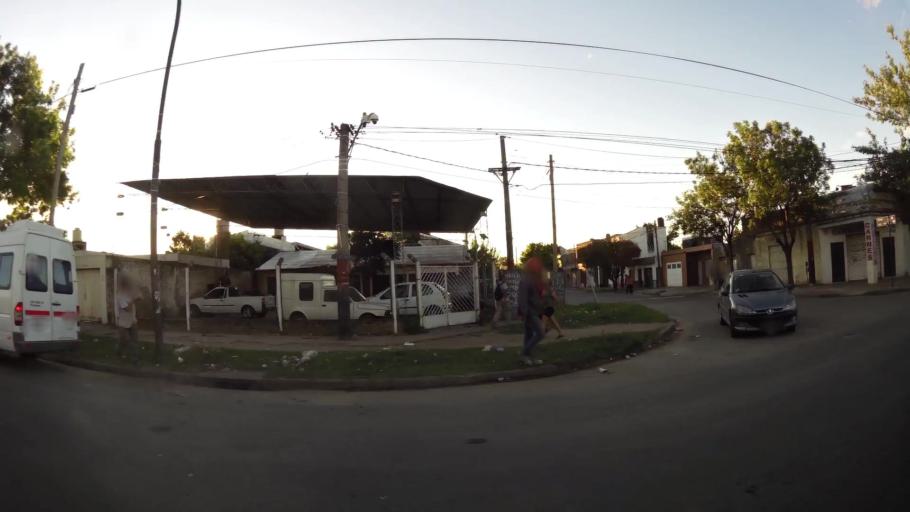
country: AR
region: Santa Fe
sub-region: Departamento de Rosario
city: Rosario
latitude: -32.9639
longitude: -60.6854
